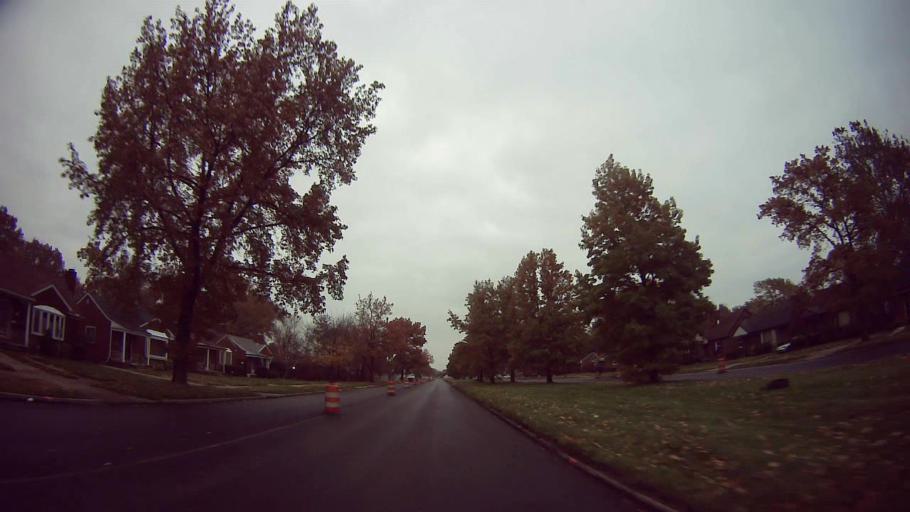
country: US
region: Michigan
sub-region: Oakland County
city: Oak Park
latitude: 42.4196
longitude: -83.2032
